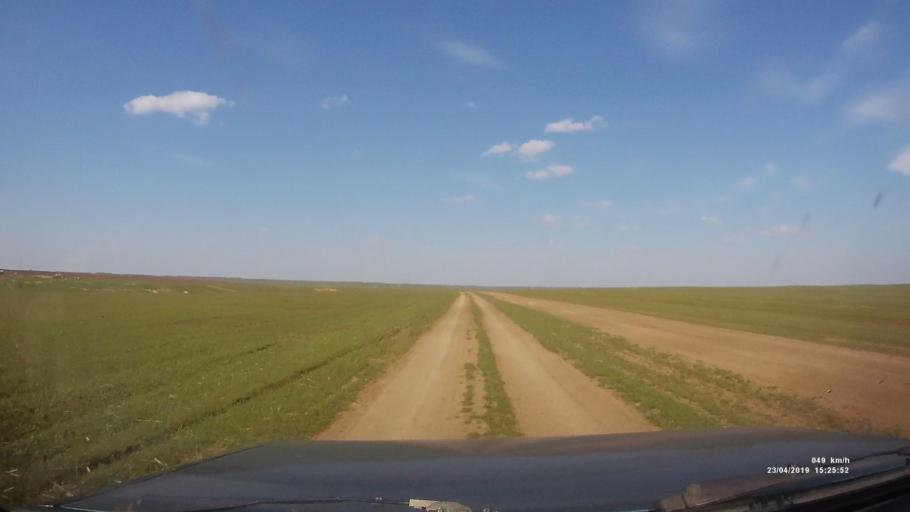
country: RU
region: Rostov
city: Remontnoye
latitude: 46.5433
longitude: 42.9850
